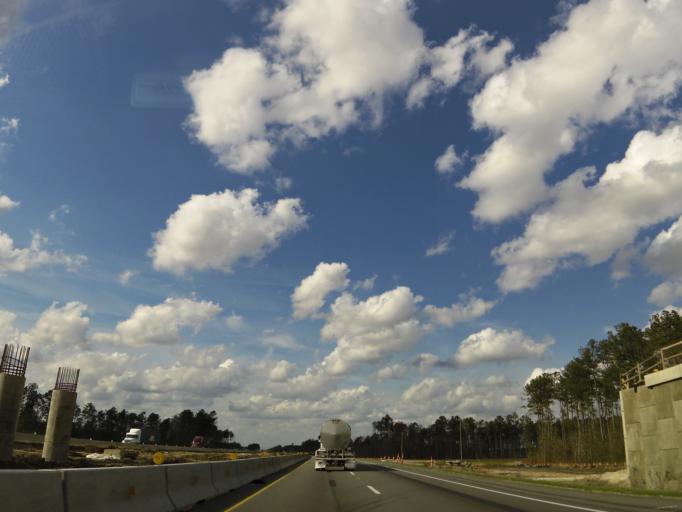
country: US
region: South Carolina
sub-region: Dorchester County
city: Summerville
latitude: 33.0532
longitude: -80.1639
